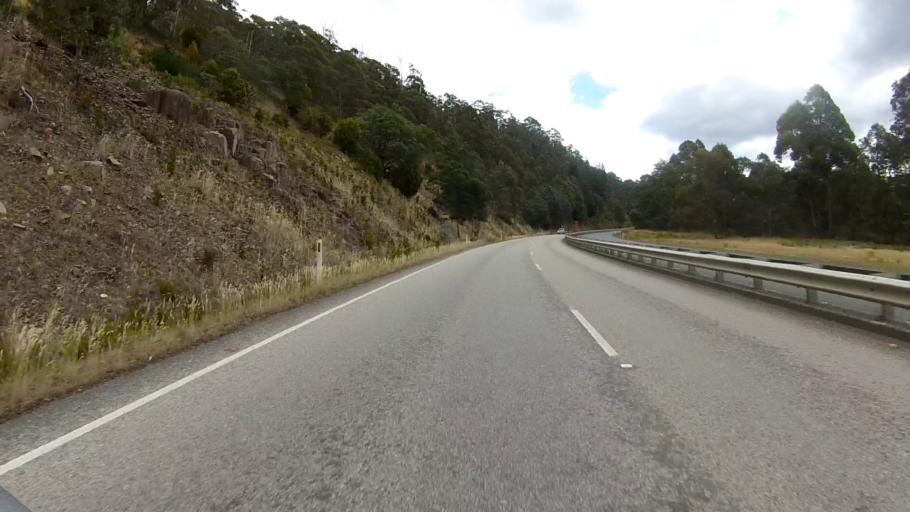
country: AU
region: Tasmania
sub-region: Kingborough
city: Margate
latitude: -42.9853
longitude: 147.1809
